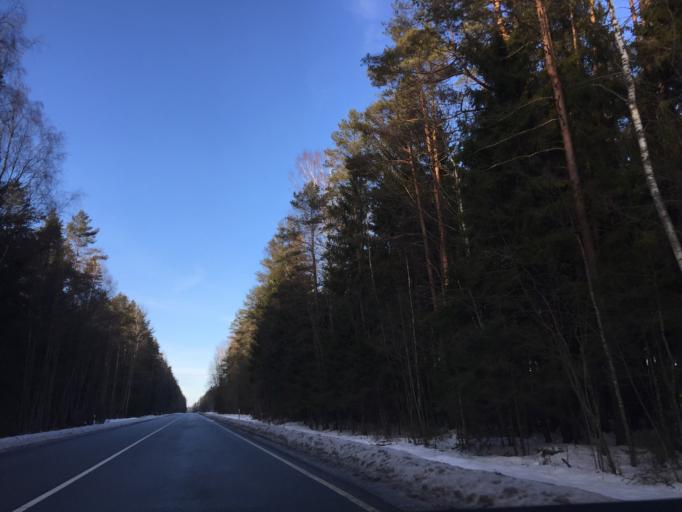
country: LV
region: Lielvarde
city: Lielvarde
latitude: 56.6706
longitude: 24.8616
